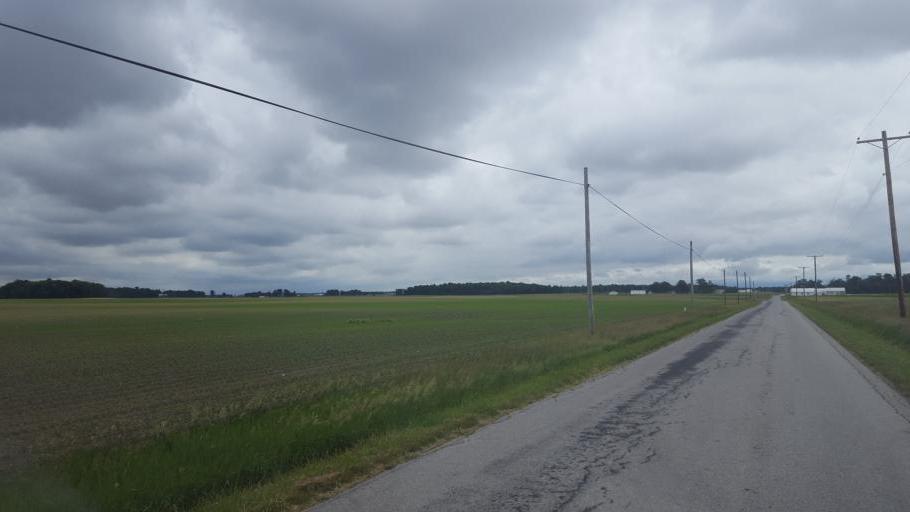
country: US
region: Ohio
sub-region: Crawford County
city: Bucyrus
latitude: 40.7615
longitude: -82.9500
